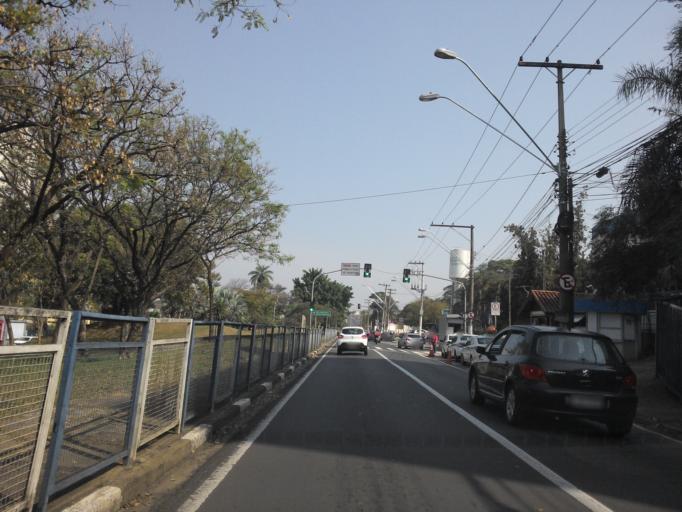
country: BR
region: Sao Paulo
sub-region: Campinas
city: Campinas
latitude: -22.9168
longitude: -47.0683
